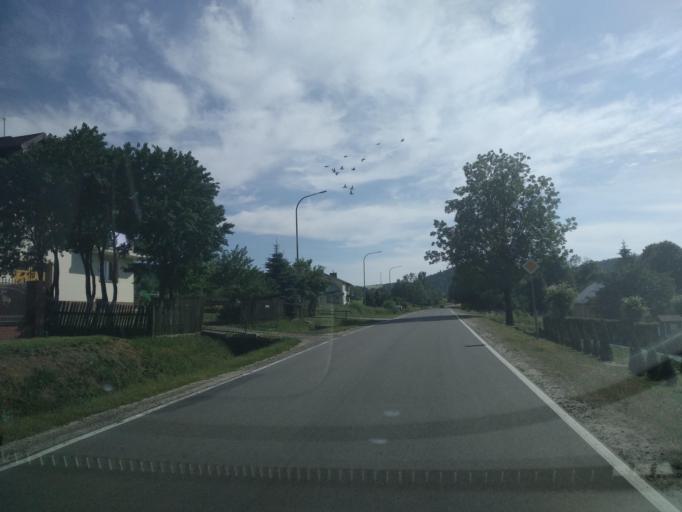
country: PL
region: Subcarpathian Voivodeship
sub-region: Powiat krosnienski
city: Jasliska
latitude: 49.5044
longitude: 21.8161
